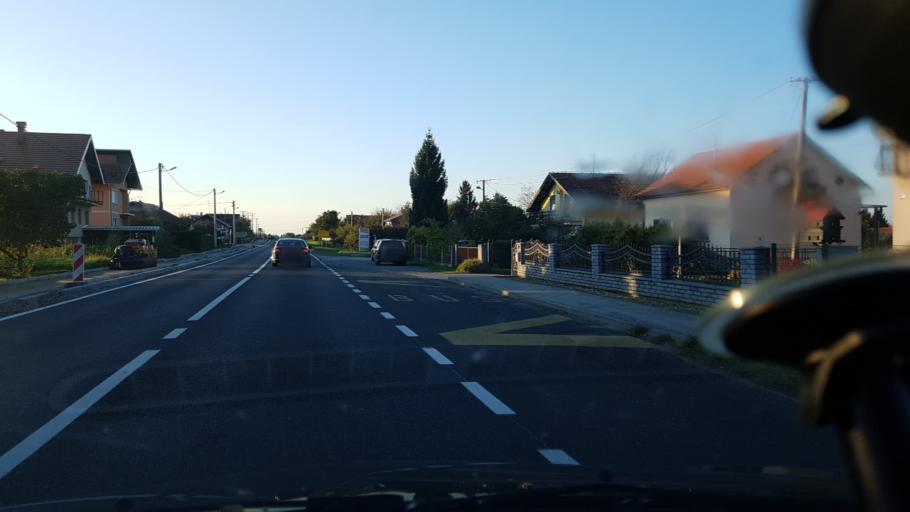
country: HR
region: Koprivnicko-Krizevacka
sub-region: Grad Koprivnica
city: Koprivnica
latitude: 46.1166
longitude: 16.8861
